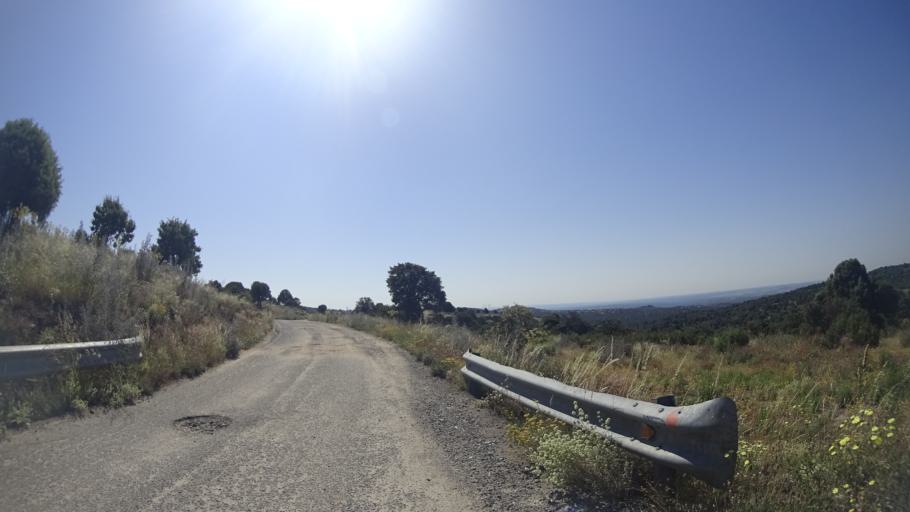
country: ES
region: Madrid
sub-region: Provincia de Madrid
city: Hoyo de Manzanares
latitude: 40.6014
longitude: -3.9021
